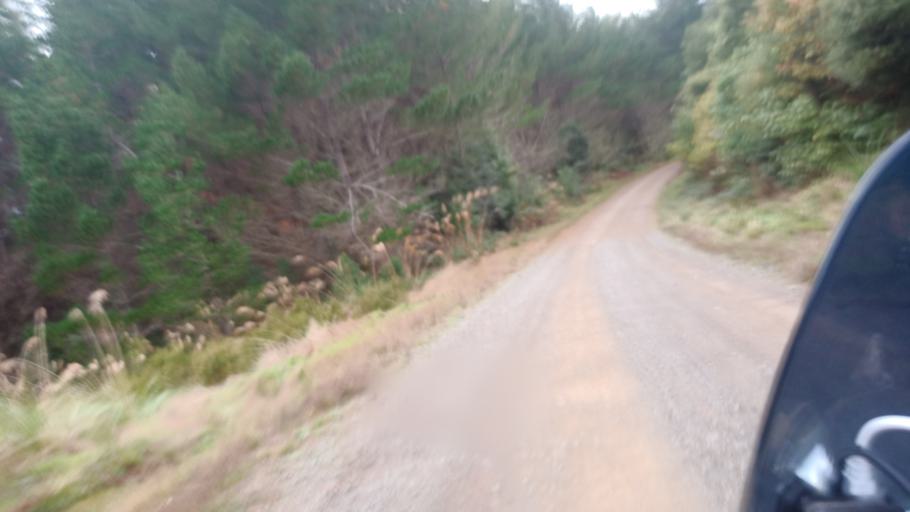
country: NZ
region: Bay of Plenty
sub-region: Whakatane District
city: Murupara
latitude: -38.6711
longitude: 176.6170
